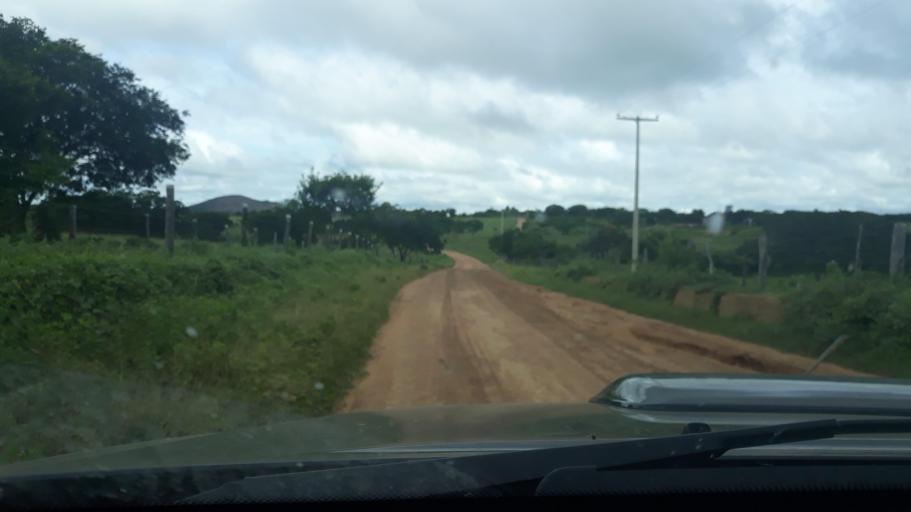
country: BR
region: Bahia
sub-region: Riacho De Santana
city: Riacho de Santana
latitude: -13.9055
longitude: -42.9034
